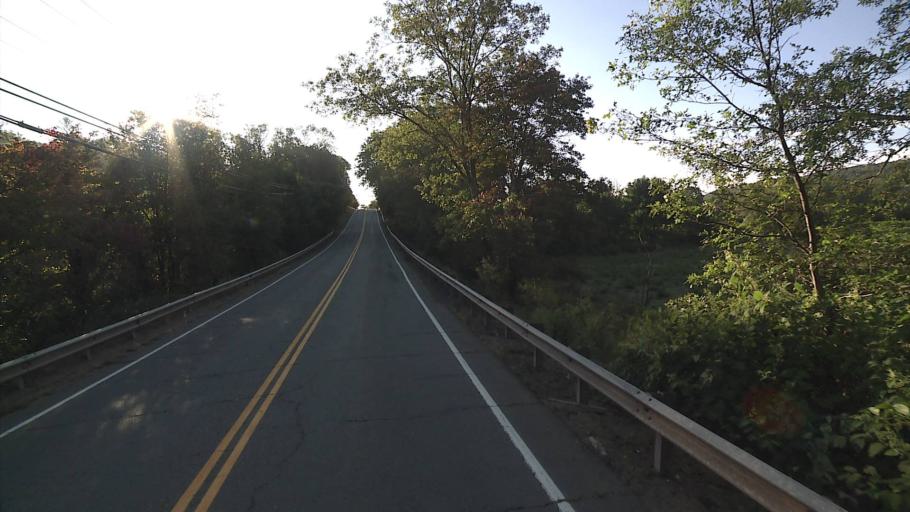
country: US
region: Connecticut
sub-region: Tolland County
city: South Coventry
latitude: 41.7995
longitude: -72.2957
